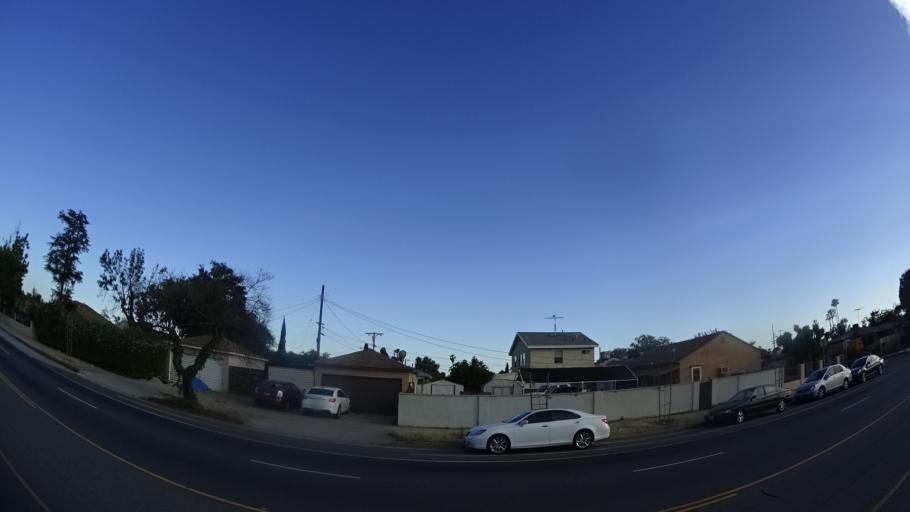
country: US
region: California
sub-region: Los Angeles County
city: North Hollywood
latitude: 34.2217
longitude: -118.4004
